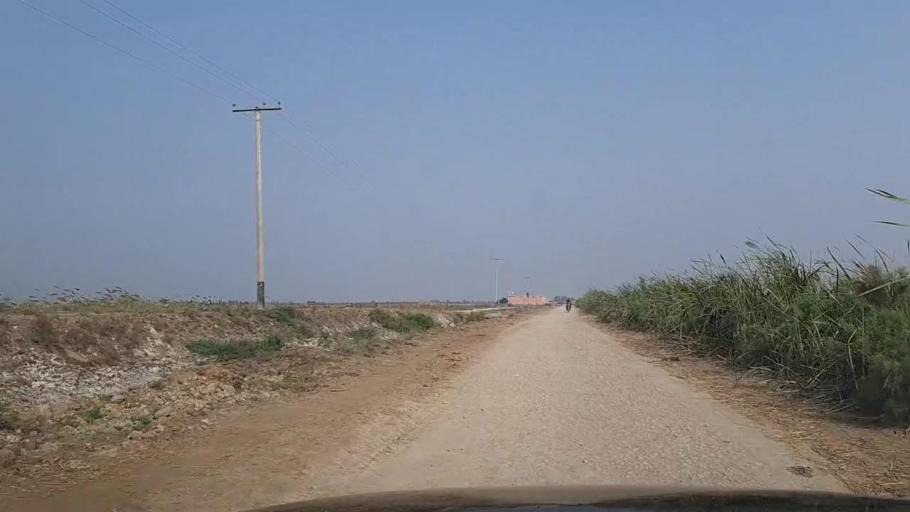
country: PK
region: Sindh
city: Thatta
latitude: 24.7558
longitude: 67.8720
